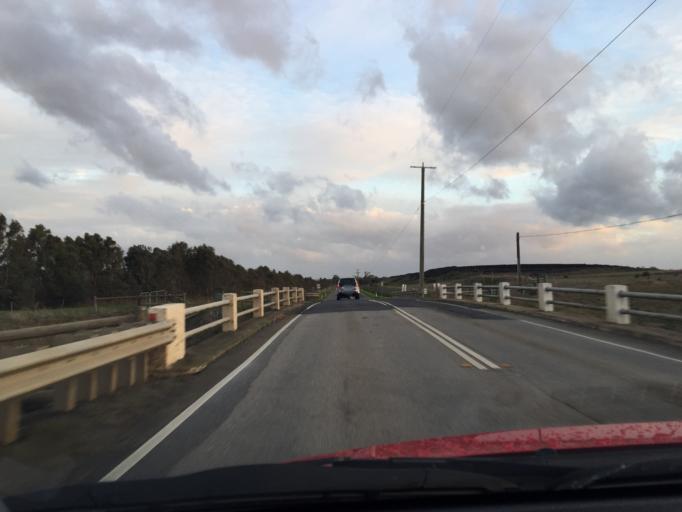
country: AU
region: Victoria
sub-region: Frankston
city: Sandhurst
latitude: -38.0413
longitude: 145.1867
